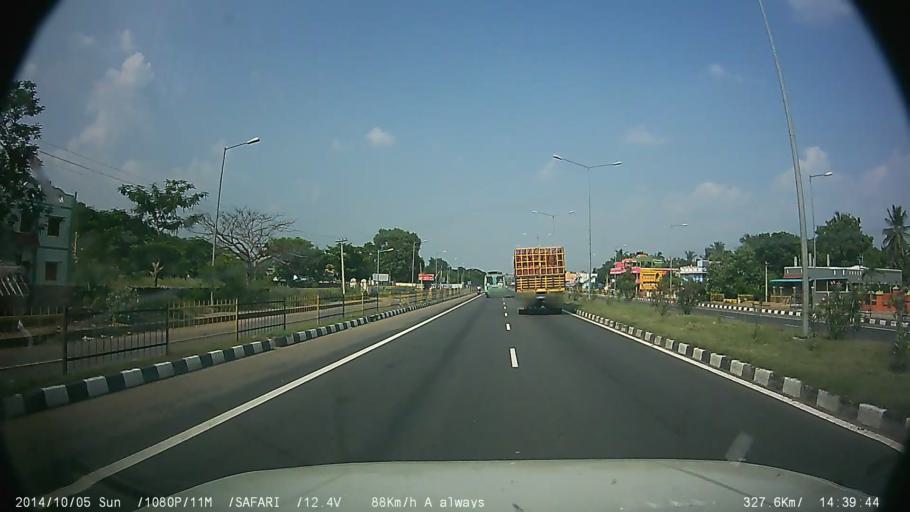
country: IN
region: Tamil Nadu
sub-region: Kancheepuram
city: Madurantakam
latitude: 12.3996
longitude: 79.8092
